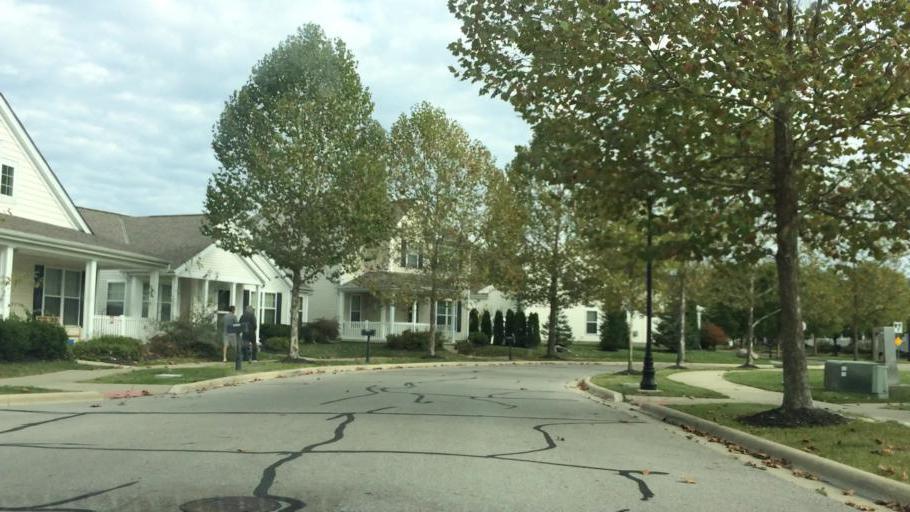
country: US
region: Ohio
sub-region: Franklin County
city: Hilliard
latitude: 40.0674
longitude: -83.1800
